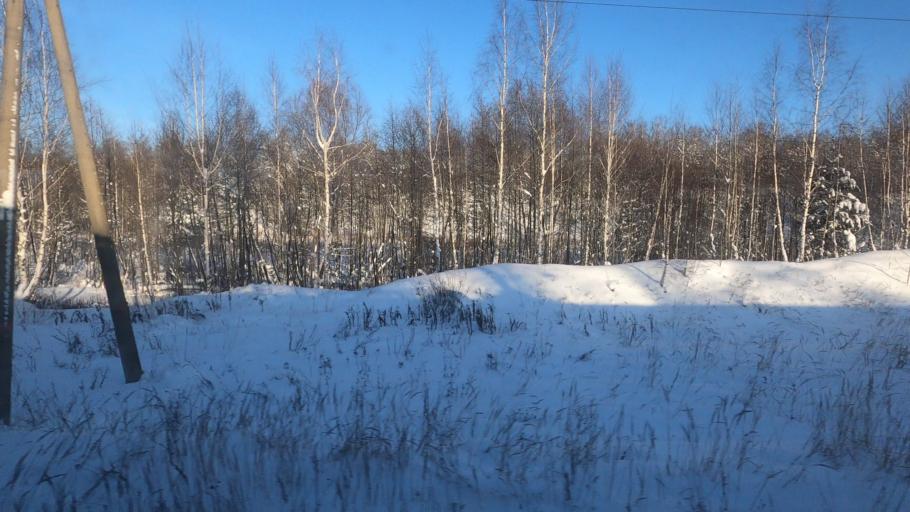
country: RU
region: Moskovskaya
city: Orud'yevo
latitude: 56.3933
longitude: 37.5009
